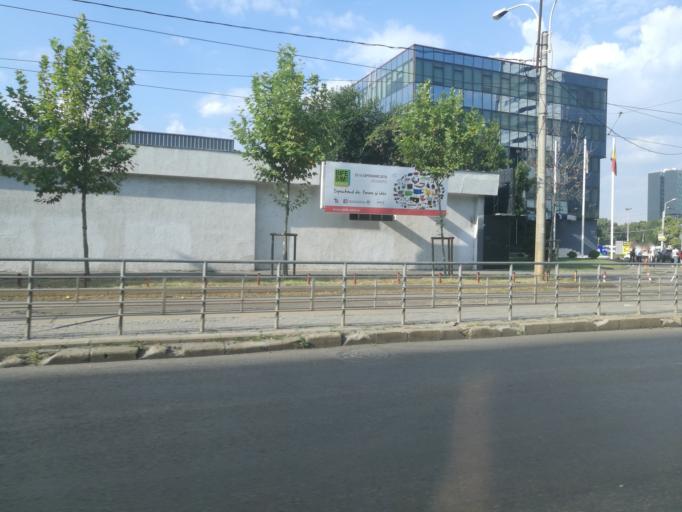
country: RO
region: Bucuresti
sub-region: Municipiul Bucuresti
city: Bucuresti
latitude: 44.4742
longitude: 26.0662
